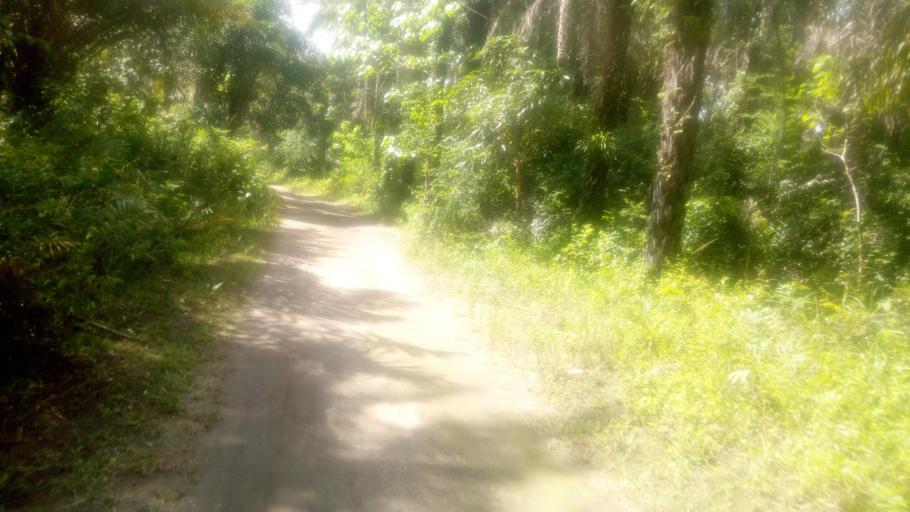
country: SL
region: Northern Province
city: Magburaka
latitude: 8.6583
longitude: -12.0690
